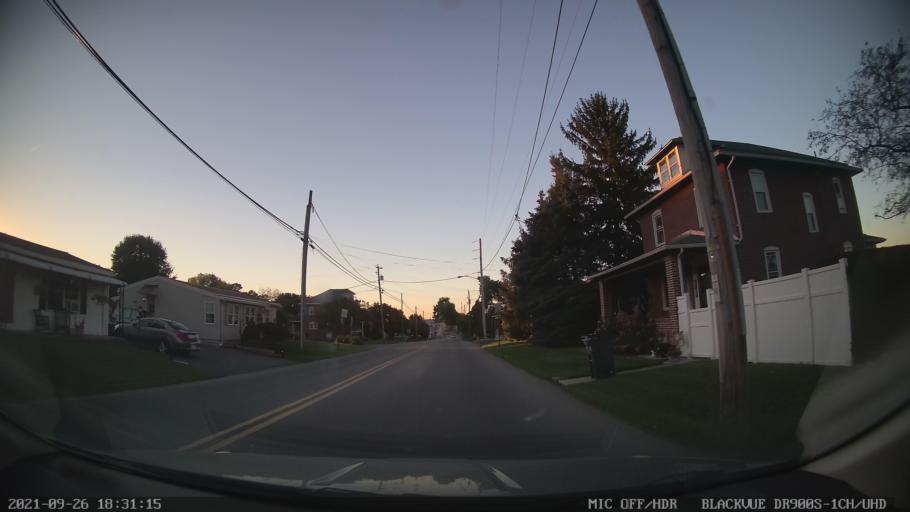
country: US
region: Pennsylvania
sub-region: Berks County
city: Kutztown
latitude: 40.4794
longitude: -75.7559
